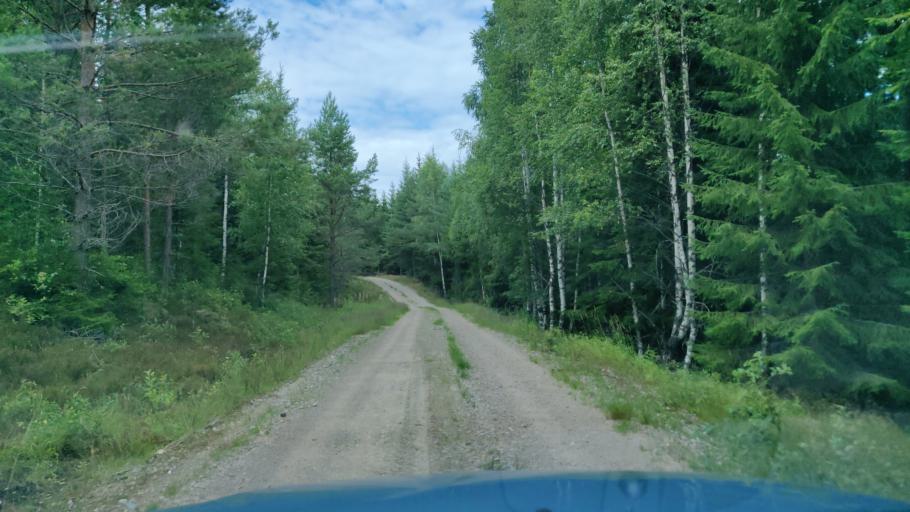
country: SE
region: Vaermland
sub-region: Hagfors Kommun
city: Hagfors
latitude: 59.9560
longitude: 13.5906
